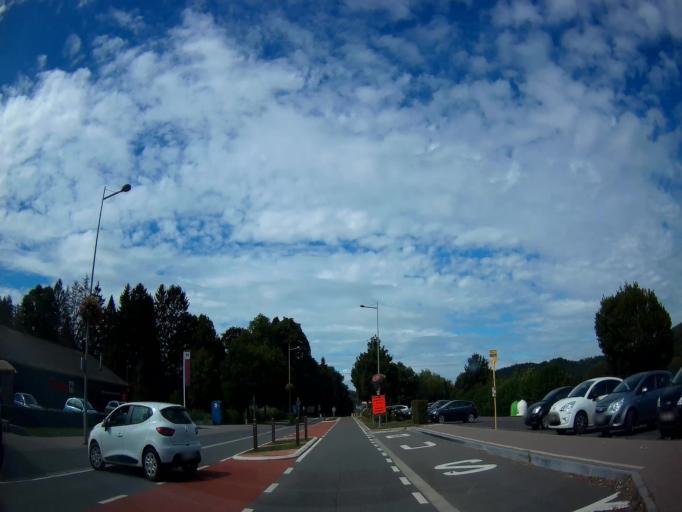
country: BE
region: Wallonia
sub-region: Province du Luxembourg
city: Rendeux
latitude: 50.2353
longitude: 5.5090
